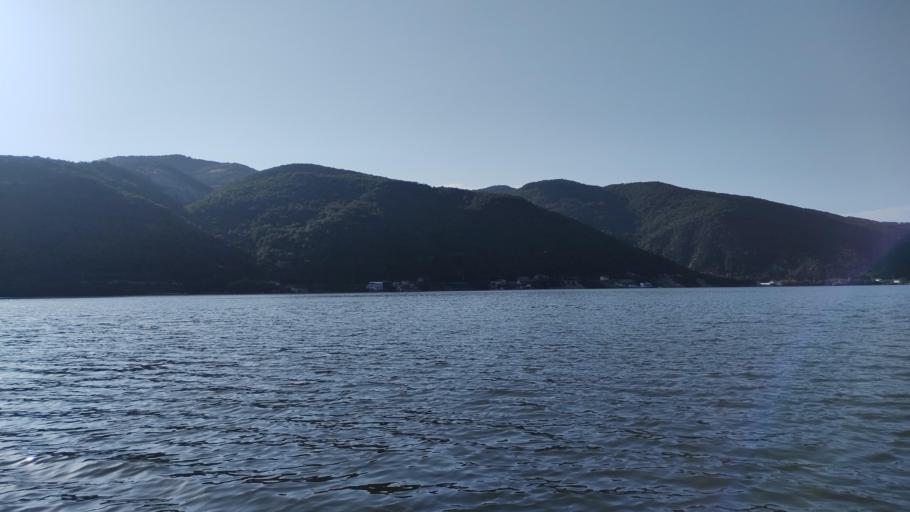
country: RO
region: Mehedinti
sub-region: Comuna Dubova
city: Dubova
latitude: 44.5599
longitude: 22.2330
